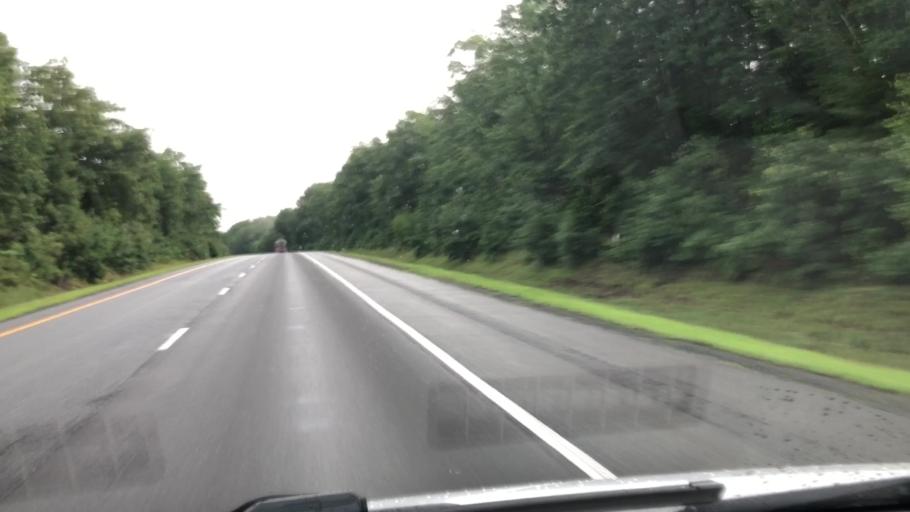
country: US
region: Massachusetts
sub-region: Franklin County
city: Greenfield
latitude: 42.5430
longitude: -72.6243
